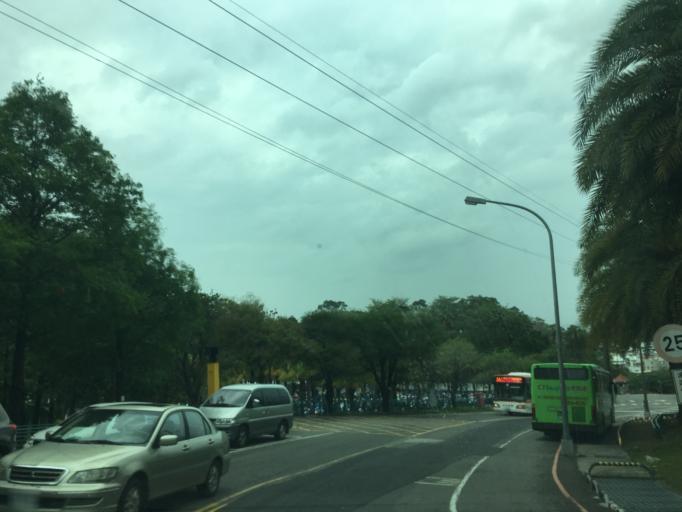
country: TW
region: Taiwan
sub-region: Taichung City
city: Taichung
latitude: 24.0693
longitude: 120.7158
